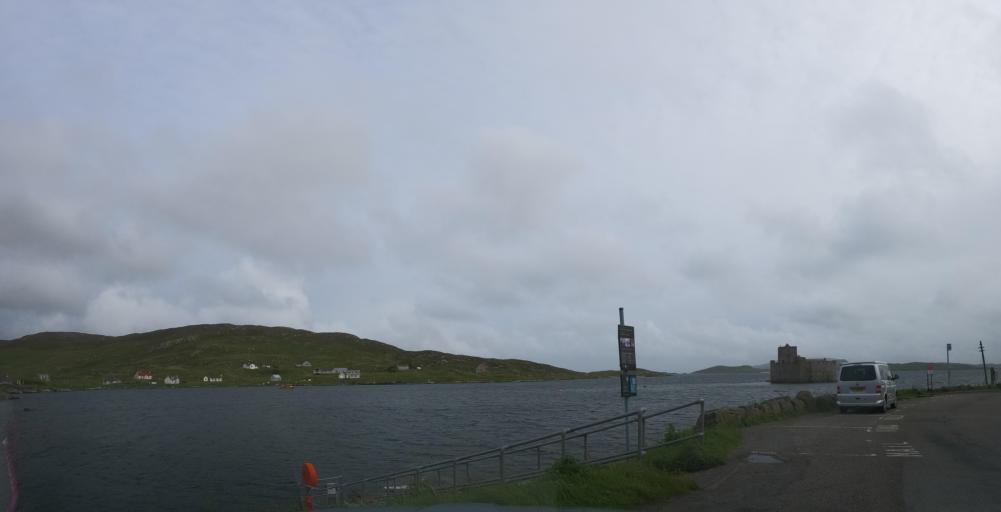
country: GB
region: Scotland
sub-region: Eilean Siar
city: Barra
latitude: 56.9543
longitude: -7.4866
